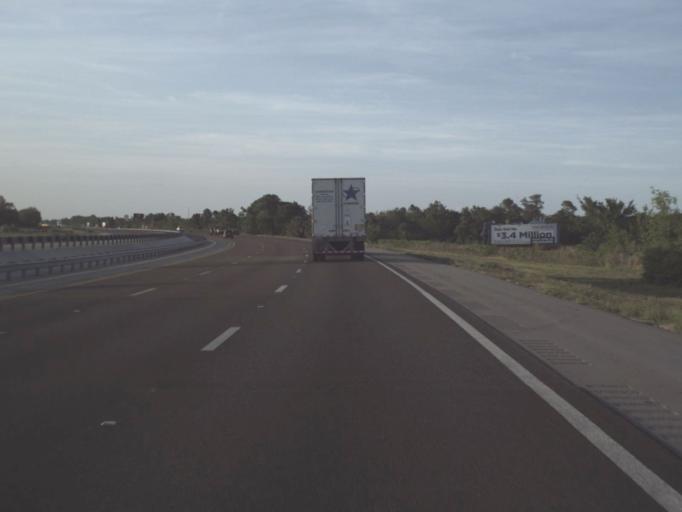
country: US
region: Florida
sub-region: Brevard County
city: Mims
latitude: 28.7372
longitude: -80.8848
